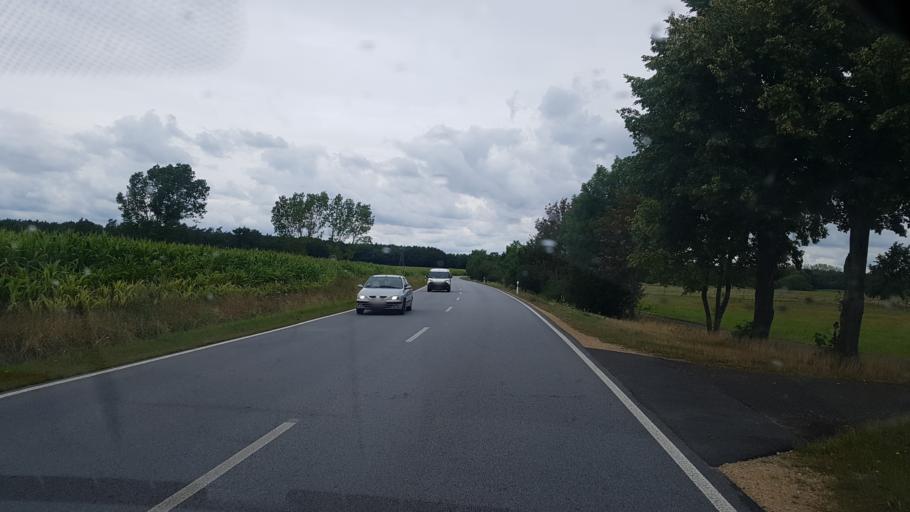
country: DE
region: Saxony
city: Niesky
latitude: 51.2603
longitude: 14.8096
